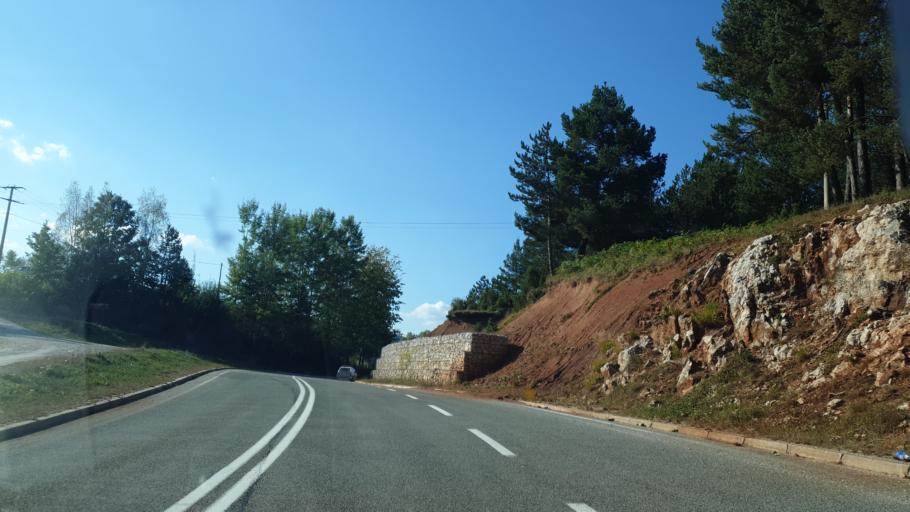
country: RS
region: Central Serbia
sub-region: Zlatiborski Okrug
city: Nova Varos
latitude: 43.5401
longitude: 19.7897
